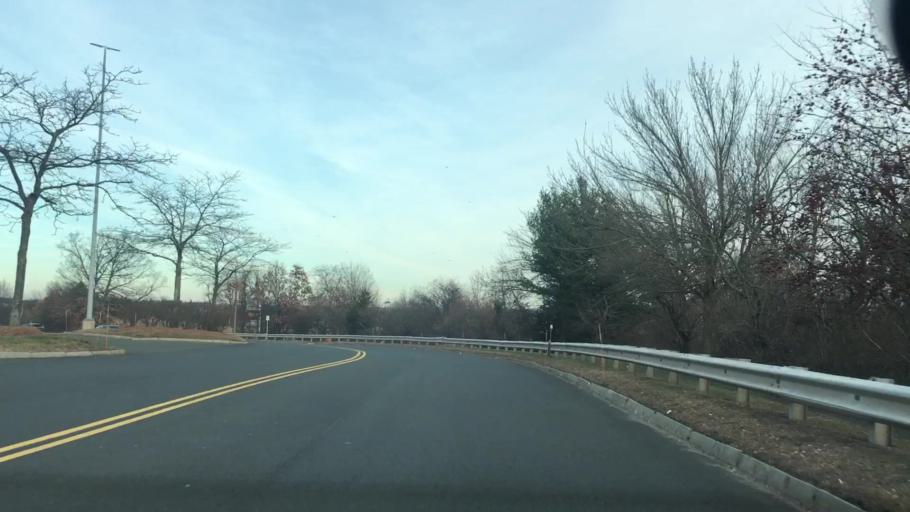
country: US
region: Connecticut
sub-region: Hartford County
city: Manchester
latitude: 41.8054
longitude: -72.5423
